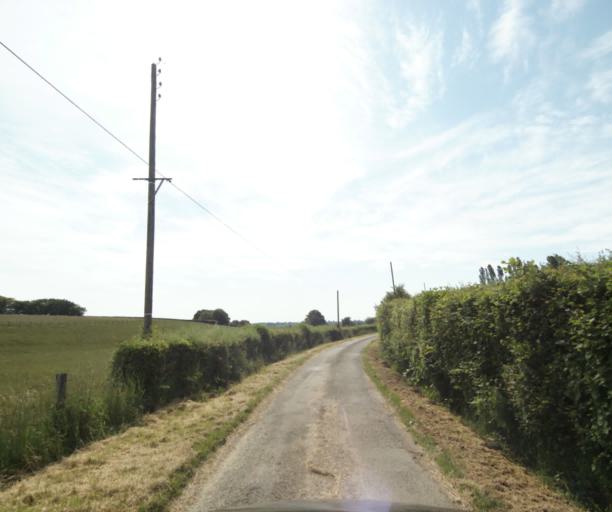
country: FR
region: Bourgogne
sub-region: Departement de Saone-et-Loire
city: Paray-le-Monial
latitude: 46.5402
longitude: 4.1244
